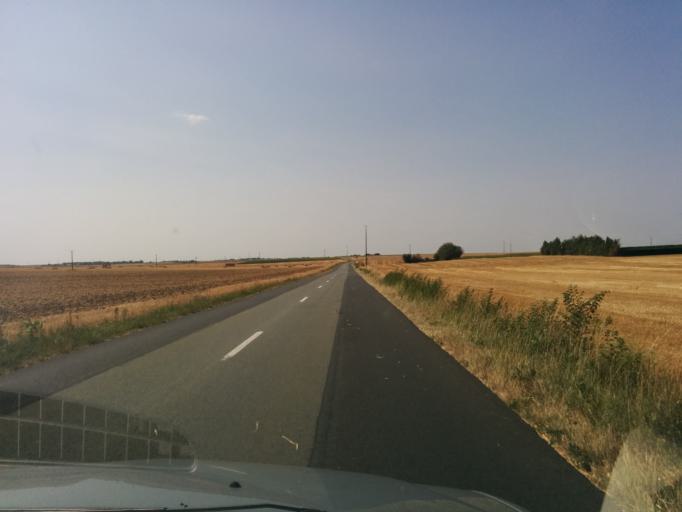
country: FR
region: Poitou-Charentes
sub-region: Departement de la Vienne
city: Mirebeau
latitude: 46.7647
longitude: 0.1531
